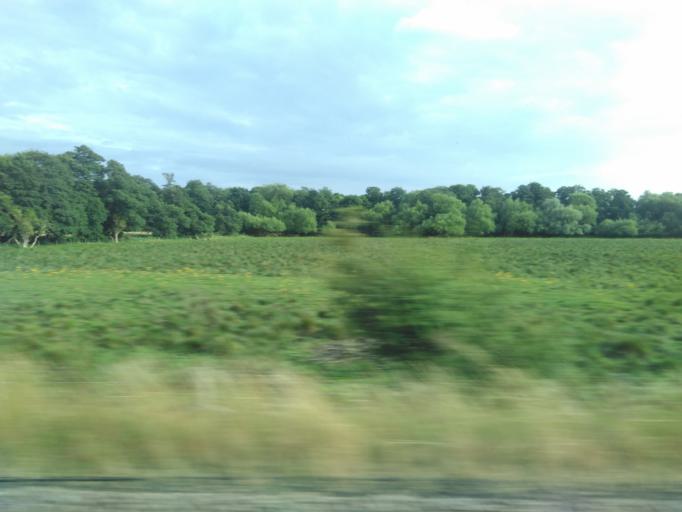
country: GB
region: England
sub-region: Norfolk
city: Weeting
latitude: 52.4535
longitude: 0.6154
